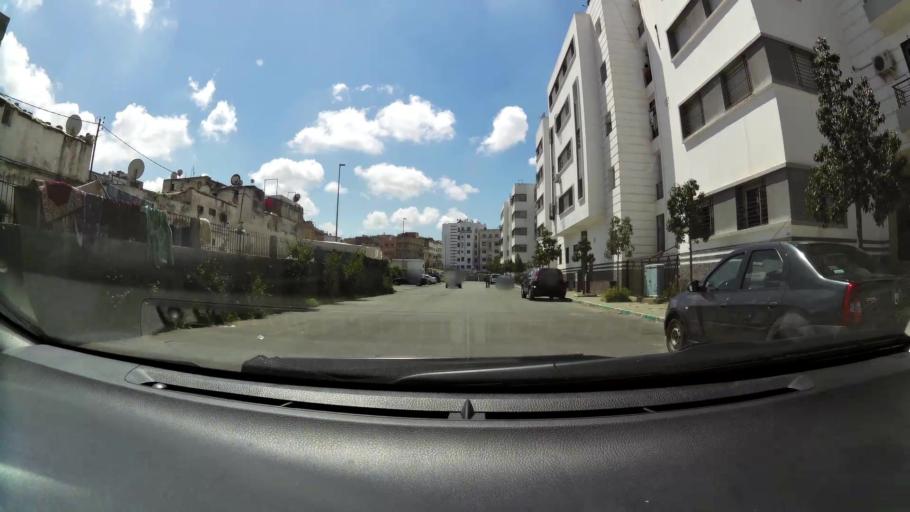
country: MA
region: Grand Casablanca
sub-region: Casablanca
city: Casablanca
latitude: 33.5618
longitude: -7.5830
